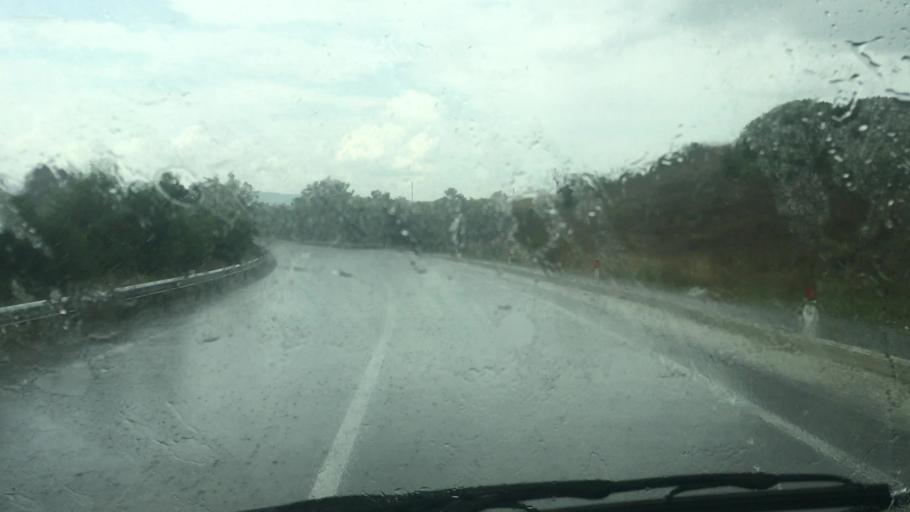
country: IT
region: Basilicate
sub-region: Provincia di Matera
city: Matera
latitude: 40.6232
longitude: 16.5855
